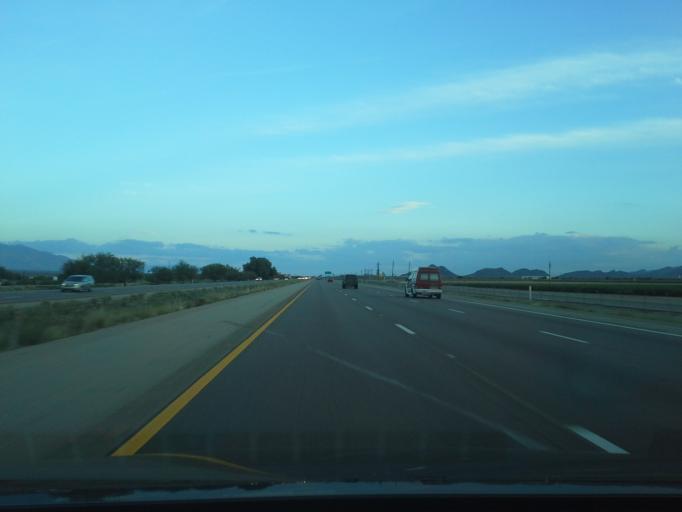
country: US
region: Arizona
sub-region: Pima County
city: Marana
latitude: 32.4415
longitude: -111.1877
